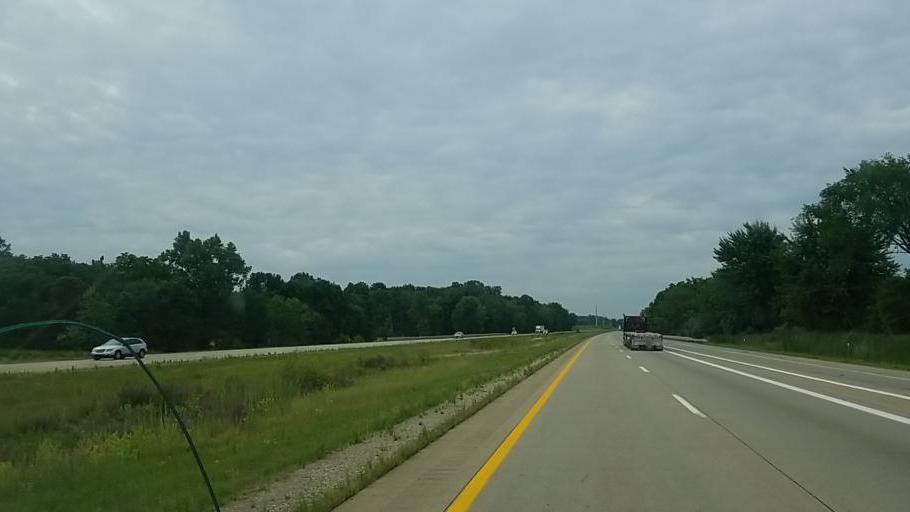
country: US
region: Michigan
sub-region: Branch County
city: Coldwater
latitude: 41.9817
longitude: -84.9721
